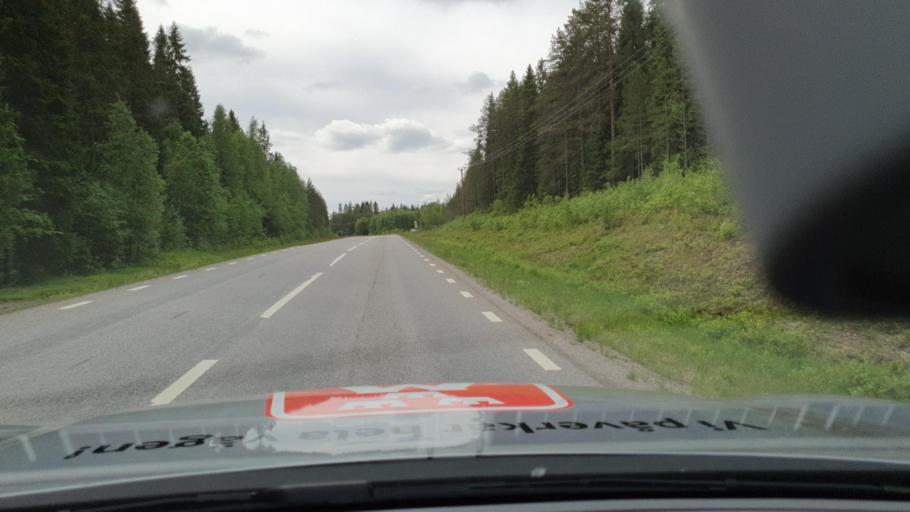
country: SE
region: Norrbotten
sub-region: Kalix Kommun
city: Kalix
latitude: 65.9151
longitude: 23.4574
